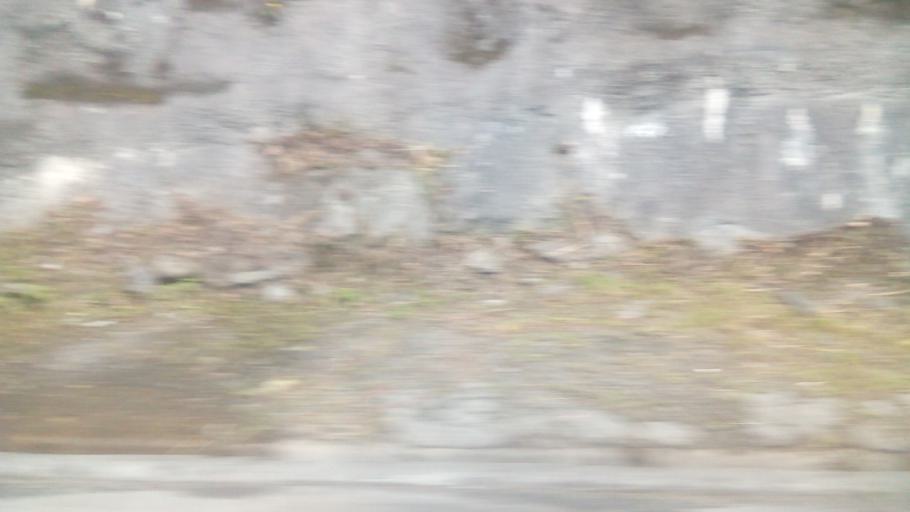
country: TW
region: Taiwan
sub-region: Yilan
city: Yilan
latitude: 24.5609
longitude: 121.4772
